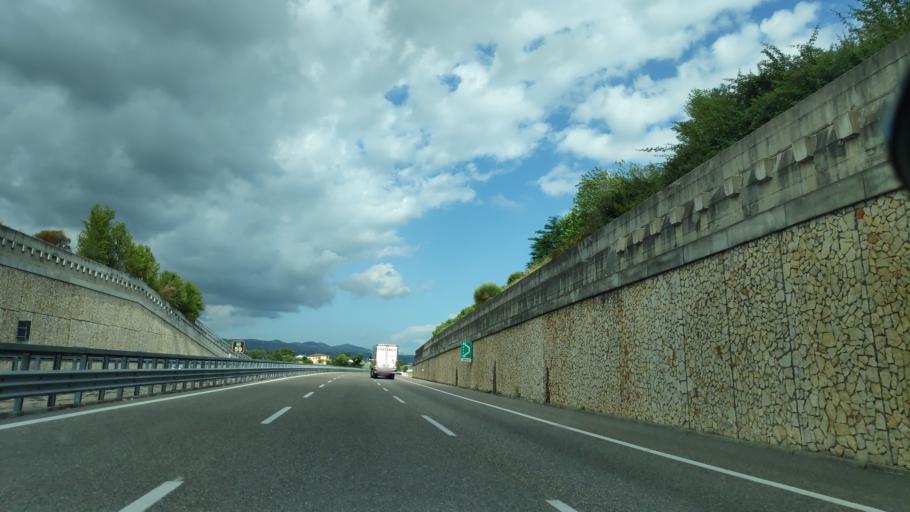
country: IT
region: Campania
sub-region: Provincia di Salerno
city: Contursi Terme
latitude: 40.6136
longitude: 15.2687
